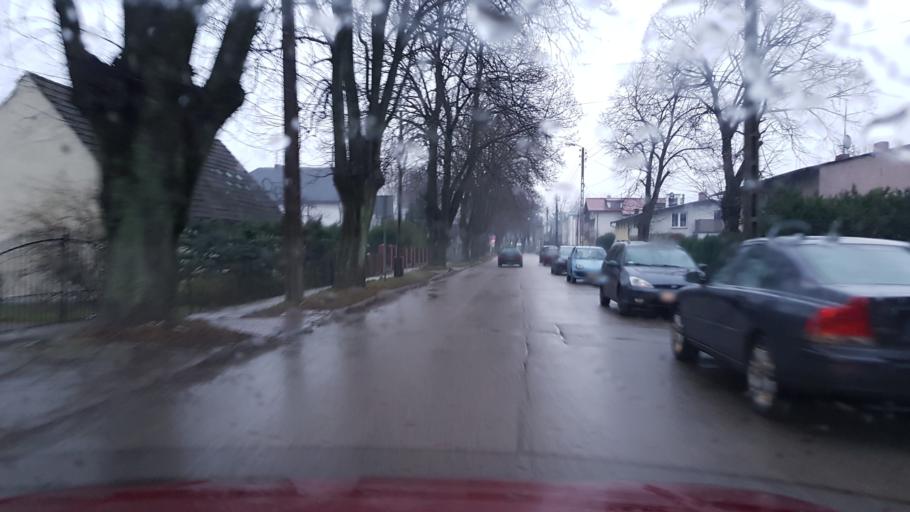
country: PL
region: West Pomeranian Voivodeship
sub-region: Koszalin
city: Koszalin
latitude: 54.1867
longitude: 16.2239
